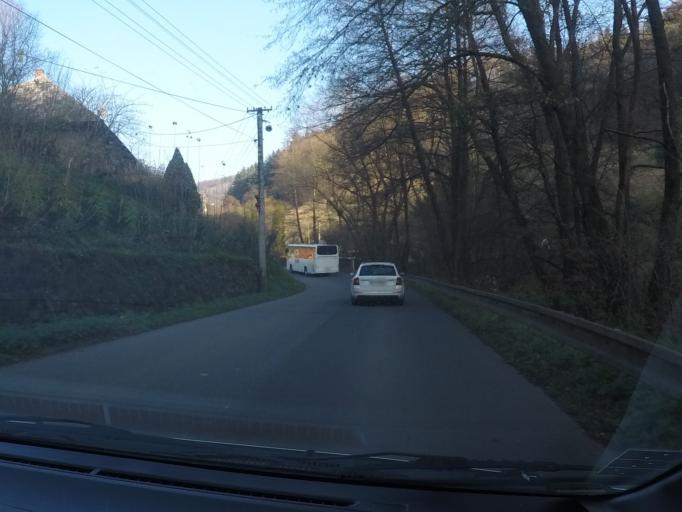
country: SK
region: Banskobystricky
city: Zarnovica
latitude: 48.4536
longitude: 18.8044
